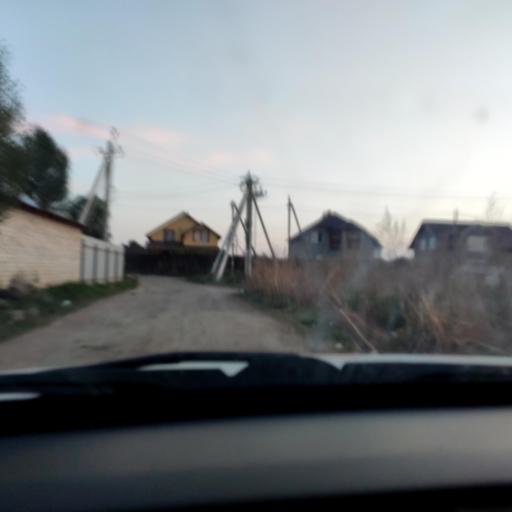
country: RU
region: Samara
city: Samara
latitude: 53.1304
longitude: 50.2417
